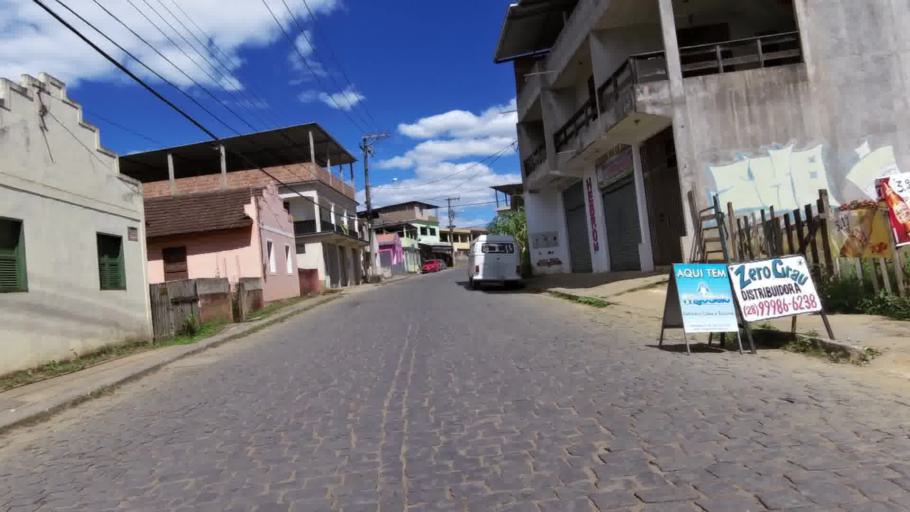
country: BR
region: Espirito Santo
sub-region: Rio Novo Do Sul
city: Rio Novo do Sul
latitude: -20.8664
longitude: -40.9400
